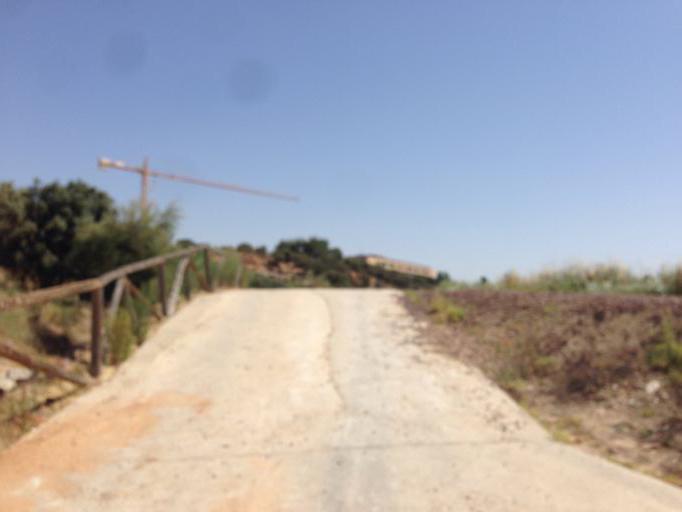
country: ES
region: Extremadura
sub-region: Provincia de Caceres
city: Berrocalejo
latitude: 39.8349
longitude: -5.3825
